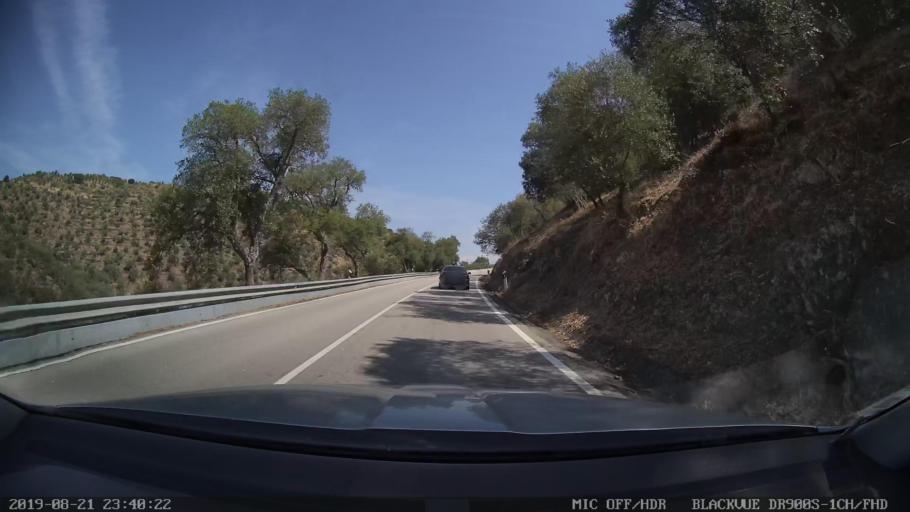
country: PT
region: Castelo Branco
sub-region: Idanha-A-Nova
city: Idanha-a-Nova
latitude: 39.8595
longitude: -7.3320
